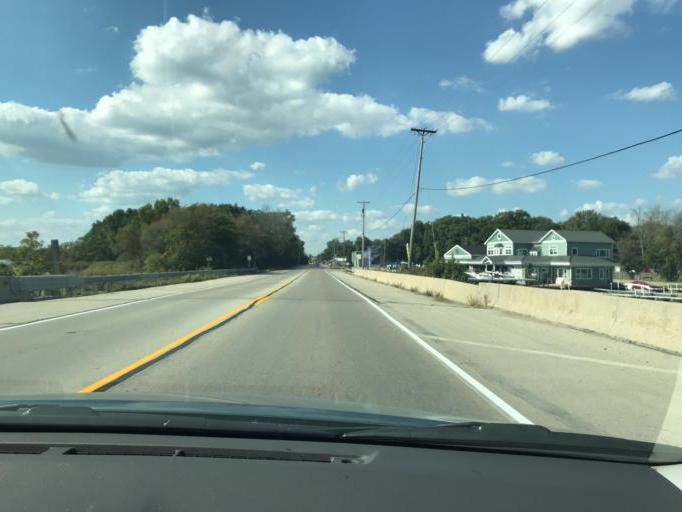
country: US
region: Wisconsin
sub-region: Walworth County
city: Williams Bay
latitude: 42.6210
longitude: -88.5826
